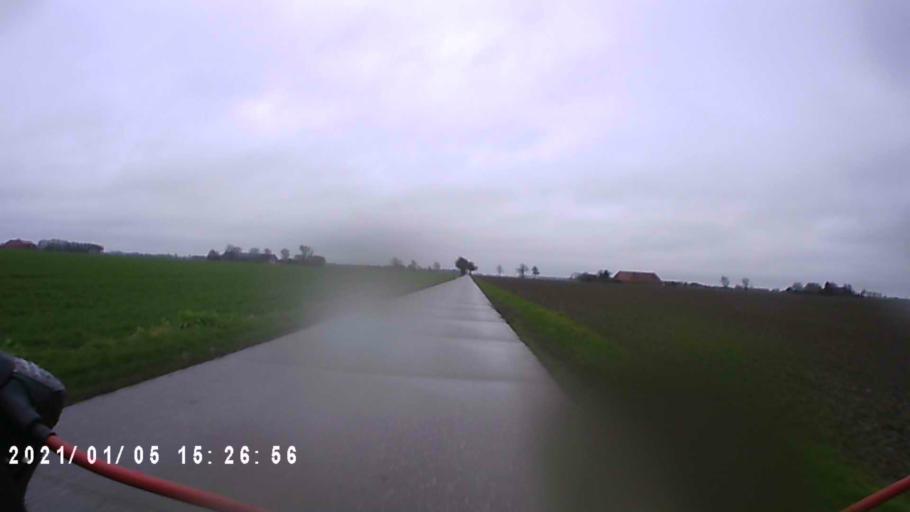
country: DE
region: Lower Saxony
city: Bunde
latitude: 53.2219
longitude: 7.1965
